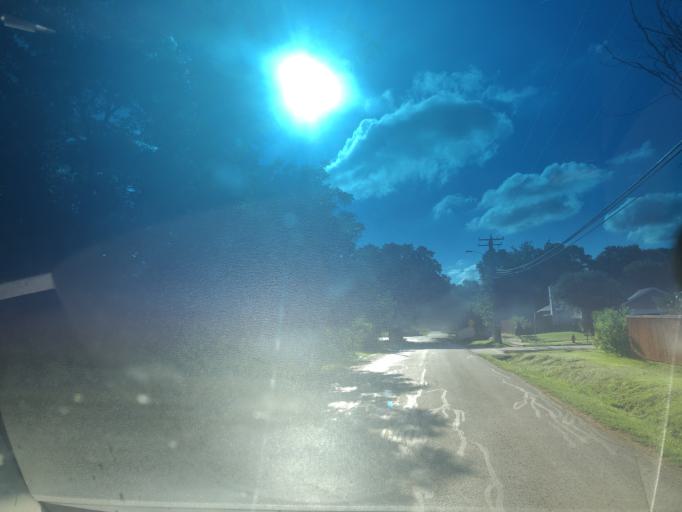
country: US
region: Texas
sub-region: Dallas County
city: Irving
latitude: 32.8107
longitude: -97.0039
